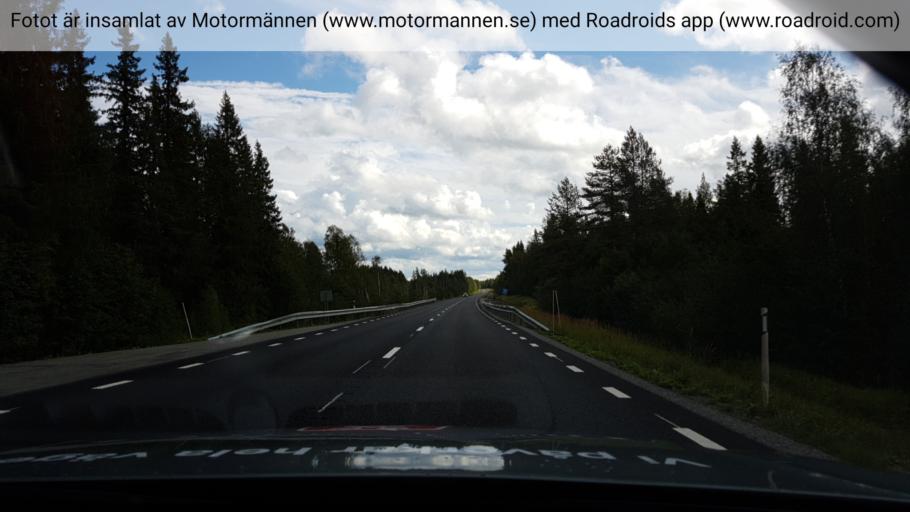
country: SE
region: Jaemtland
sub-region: OEstersunds Kommun
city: Brunflo
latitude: 63.2021
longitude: 14.9286
